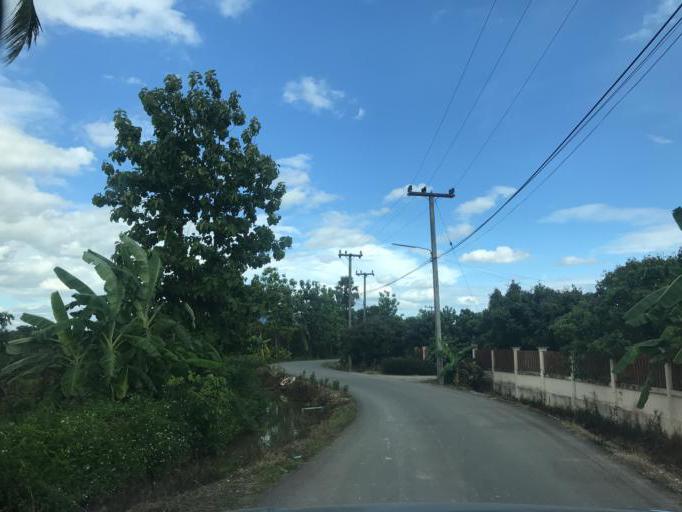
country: TH
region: Chiang Mai
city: Mae Wang
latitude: 18.5652
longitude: 98.8376
